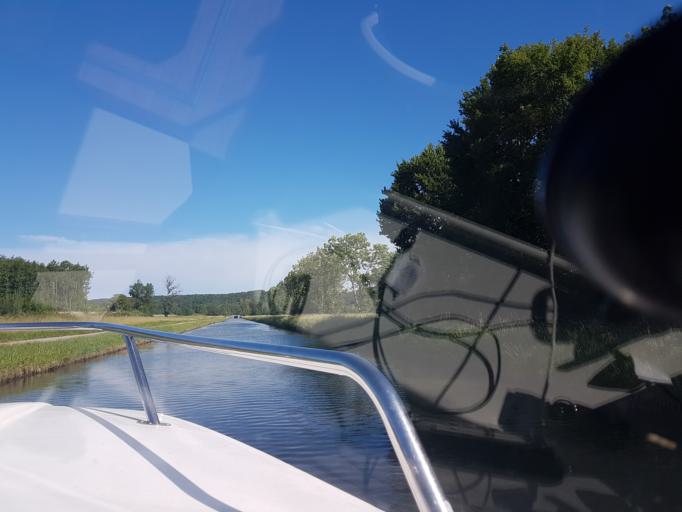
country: FR
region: Bourgogne
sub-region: Departement de la Nievre
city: Clamecy
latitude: 47.5330
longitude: 3.6144
